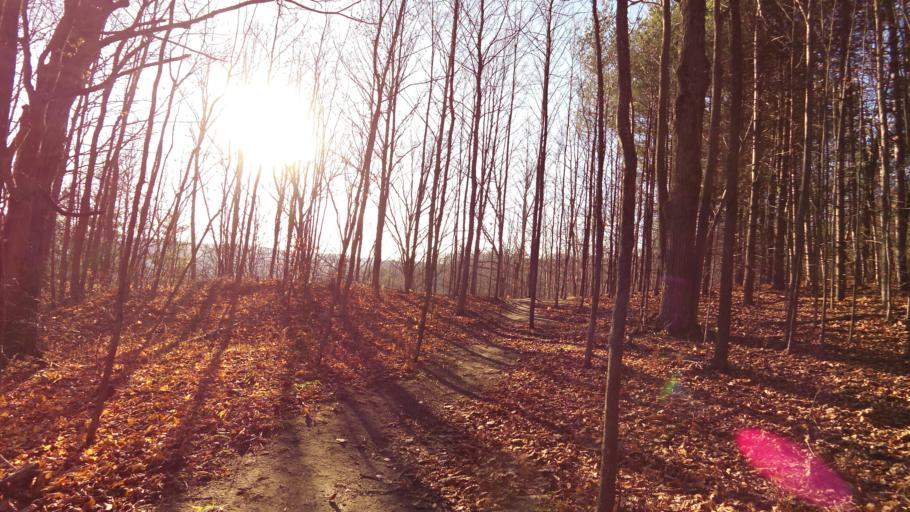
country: CA
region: Ontario
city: Orangeville
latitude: 43.9910
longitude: -80.0533
